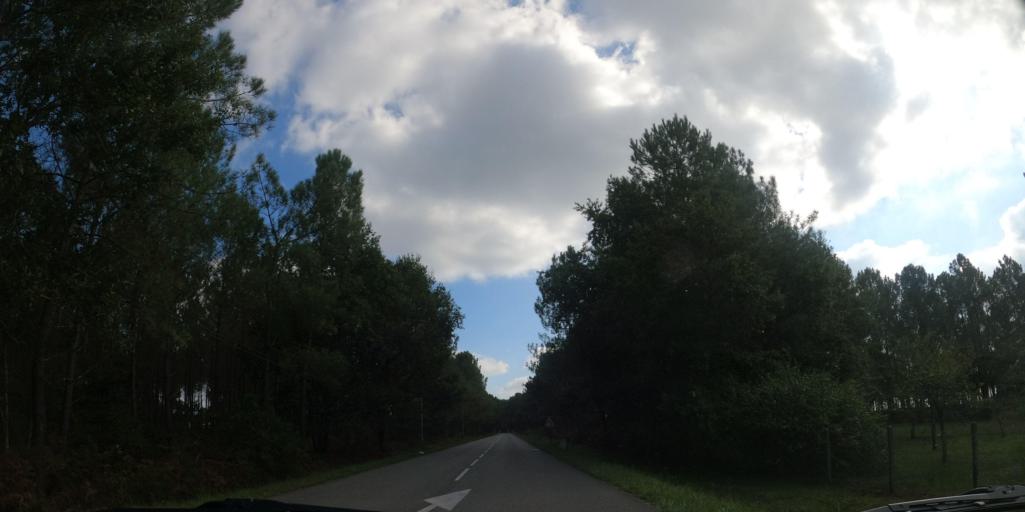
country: FR
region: Aquitaine
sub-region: Departement des Landes
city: Soustons
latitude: 43.7393
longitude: -1.2969
